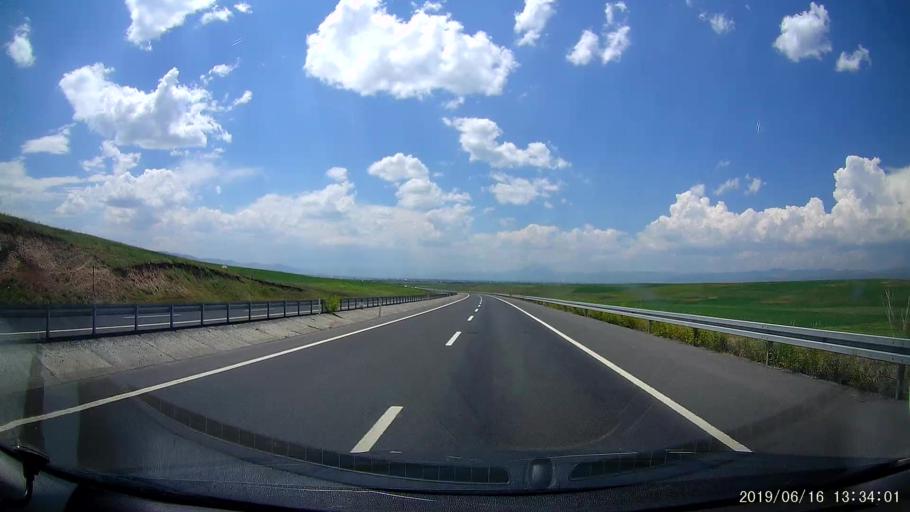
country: TR
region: Agri
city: Agri
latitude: 39.7106
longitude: 43.1383
